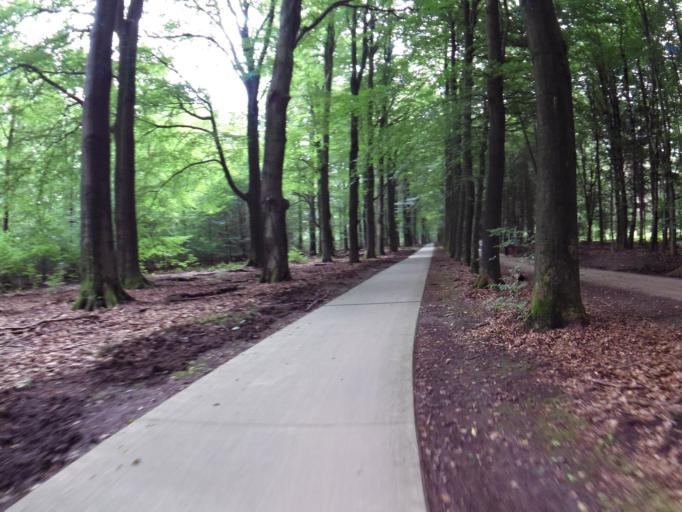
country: NL
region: Gelderland
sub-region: Gemeente Rheden
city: De Steeg
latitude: 52.0384
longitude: 6.0562
